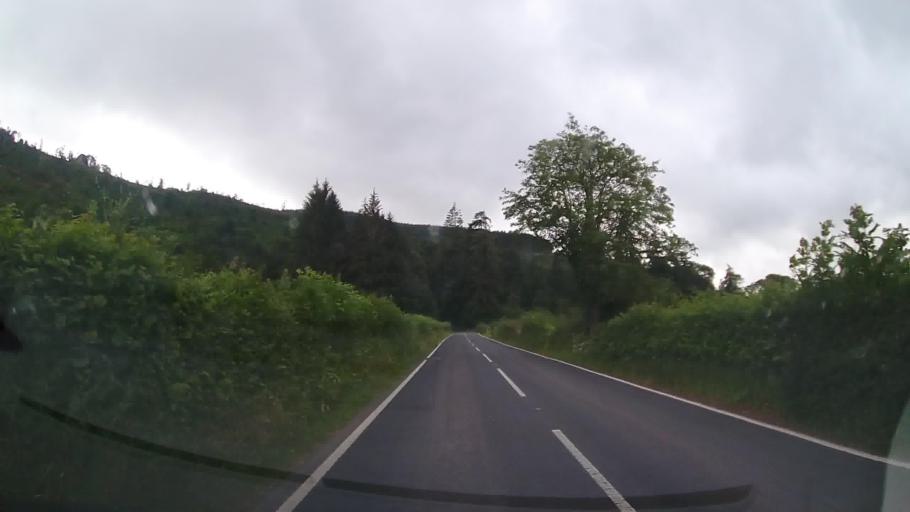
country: GB
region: Wales
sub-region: Denbighshire
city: Llandrillo
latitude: 52.9218
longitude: -3.4589
